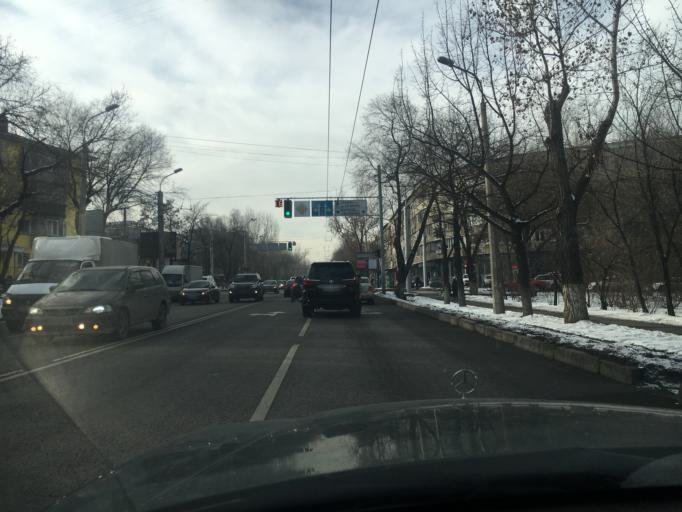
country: KZ
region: Almaty Qalasy
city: Almaty
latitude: 43.2326
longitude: 76.9011
